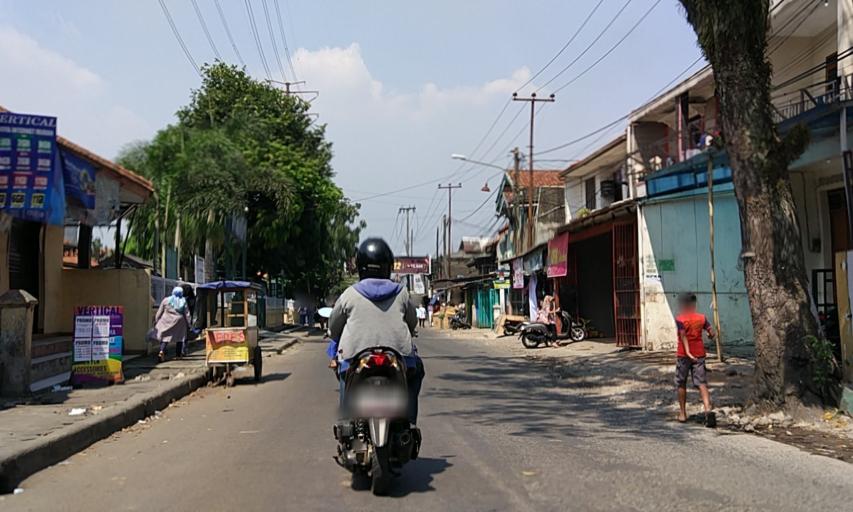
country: ID
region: West Java
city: Margahayukencana
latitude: -6.9263
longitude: 107.5643
